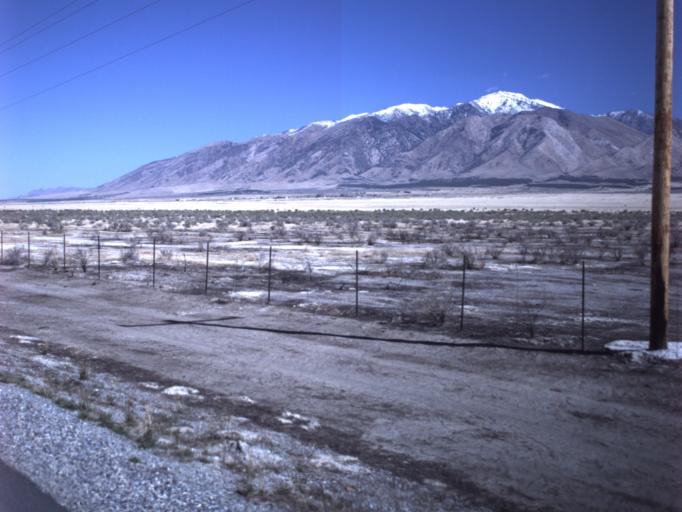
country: US
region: Utah
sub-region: Tooele County
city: Grantsville
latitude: 40.3675
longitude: -112.7462
